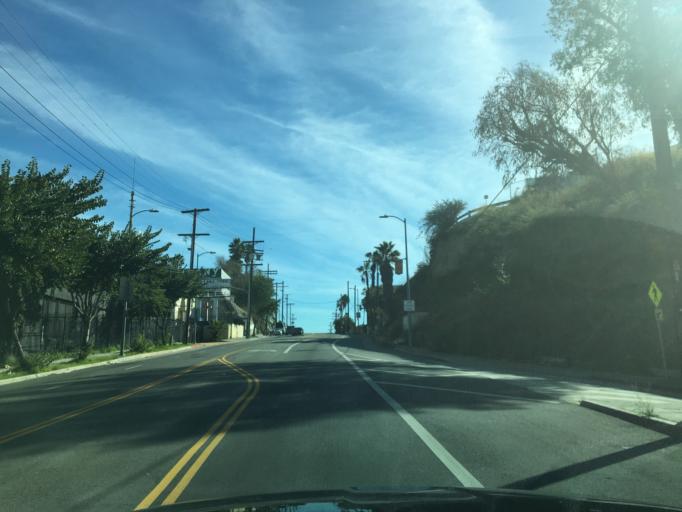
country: US
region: California
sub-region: Los Angeles County
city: Silver Lake
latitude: 34.0765
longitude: -118.2838
